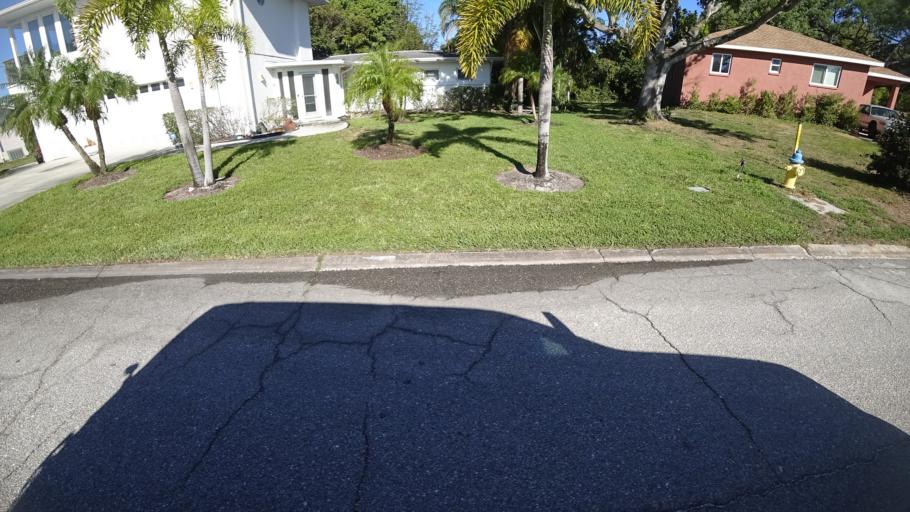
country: US
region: Florida
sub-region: Manatee County
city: Bayshore Gardens
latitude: 27.4237
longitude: -82.5951
